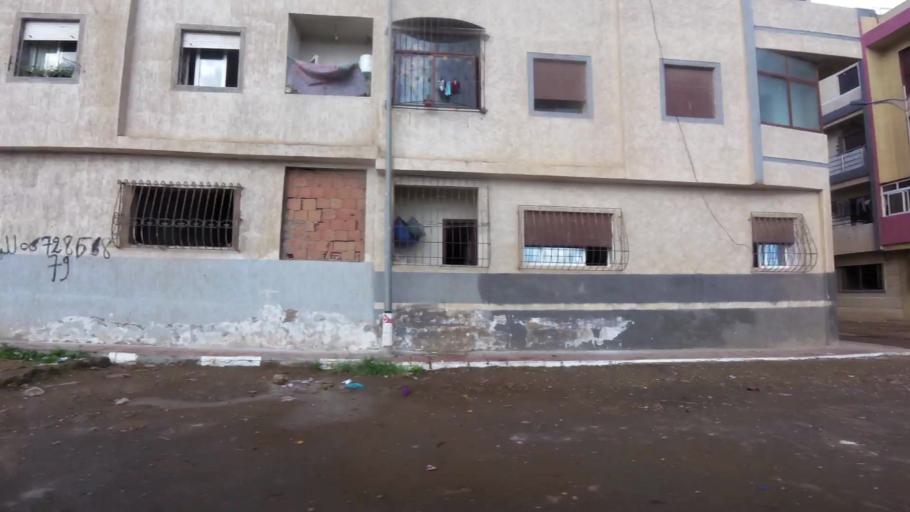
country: MA
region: Grand Casablanca
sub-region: Nouaceur
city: Bouskoura
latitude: 33.5378
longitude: -7.7020
